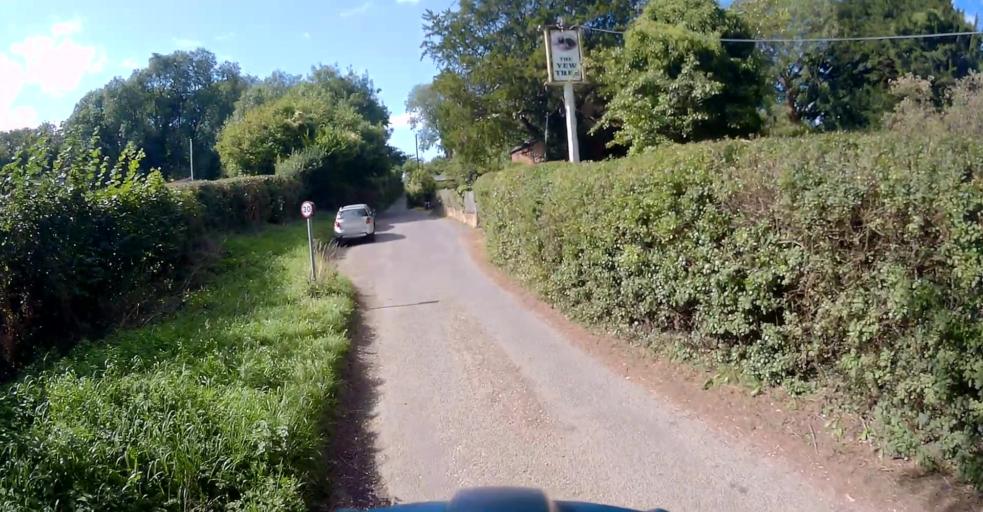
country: GB
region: England
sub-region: Hampshire
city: Four Marks
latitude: 51.1530
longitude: -1.0910
